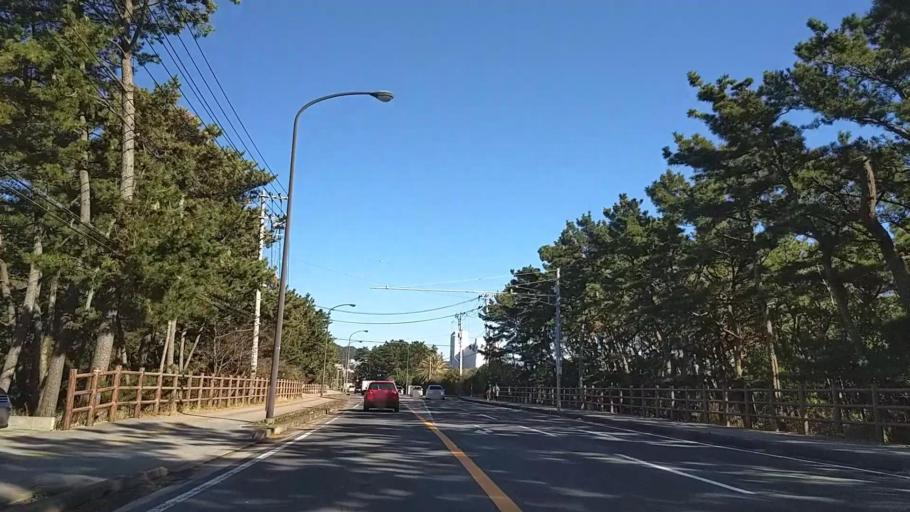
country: JP
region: Chiba
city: Kawaguchi
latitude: 35.1125
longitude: 140.1142
